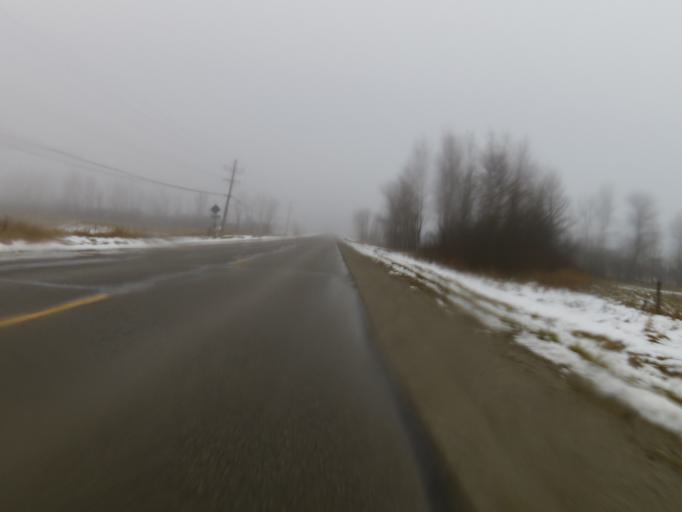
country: CA
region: Ontario
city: Perth
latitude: 44.8594
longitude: -76.3427
